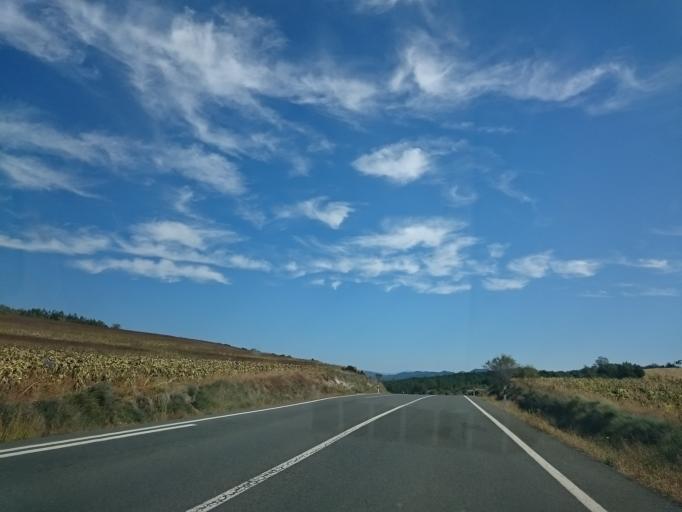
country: ES
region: Aragon
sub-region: Provincia de Huesca
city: Castigaleu
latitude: 42.1386
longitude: 0.6443
